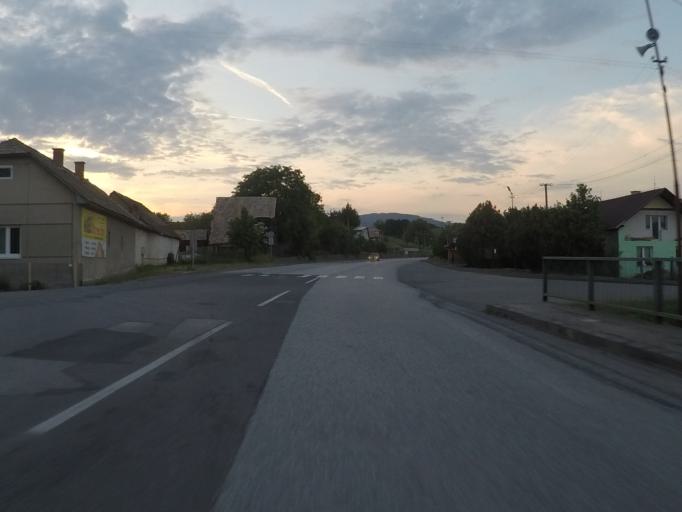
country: SK
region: Banskobystricky
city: Rimavska Sobota
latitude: 48.4790
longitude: 19.9448
